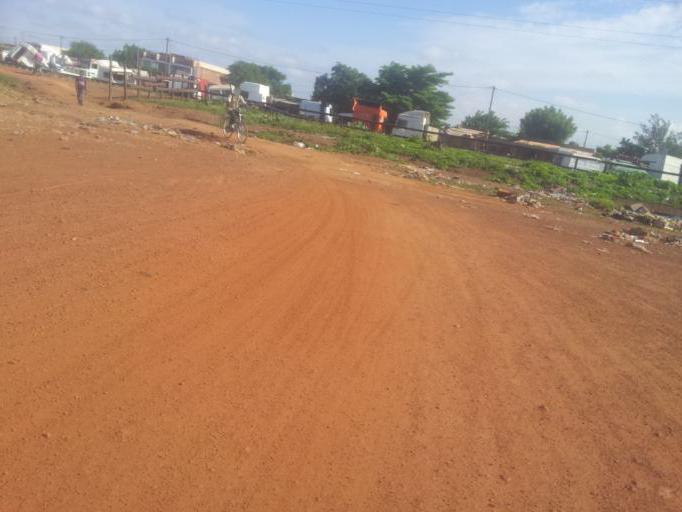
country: BF
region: Centre
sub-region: Kadiogo Province
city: Ouagadougou
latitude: 12.3699
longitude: -1.5555
